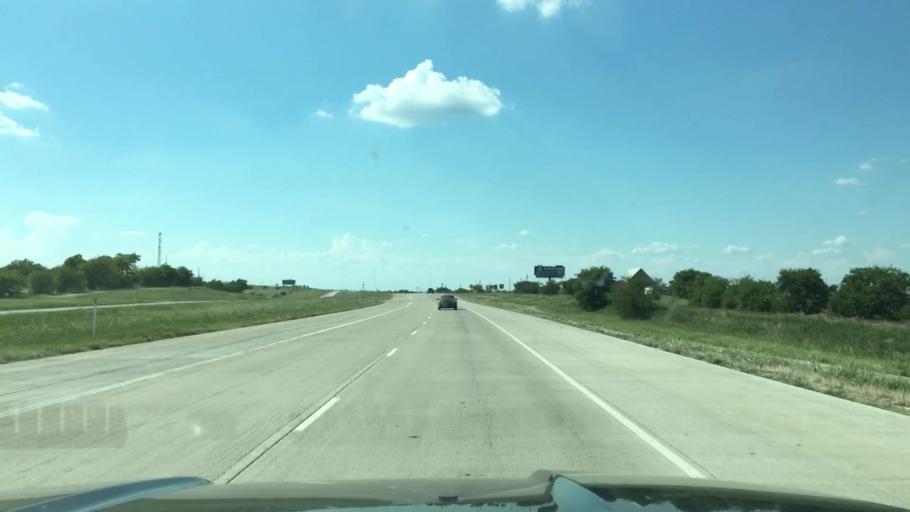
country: US
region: Texas
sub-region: Wise County
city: New Fairview
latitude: 33.1485
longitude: -97.5046
